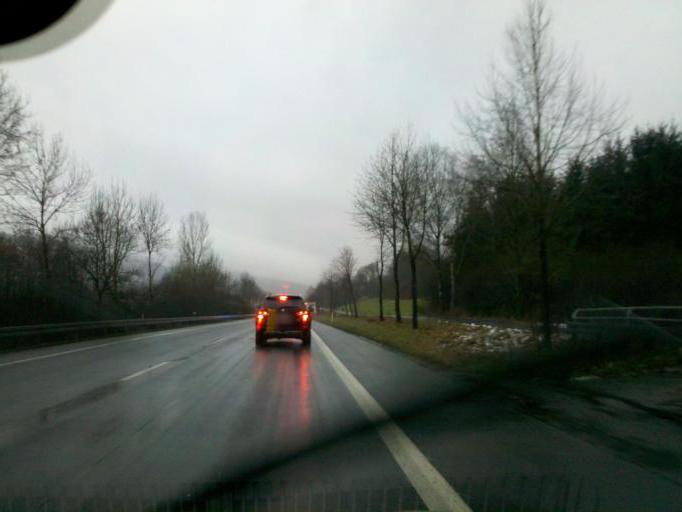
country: DE
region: Hesse
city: Dillenburg
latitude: 50.7970
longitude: 8.3327
